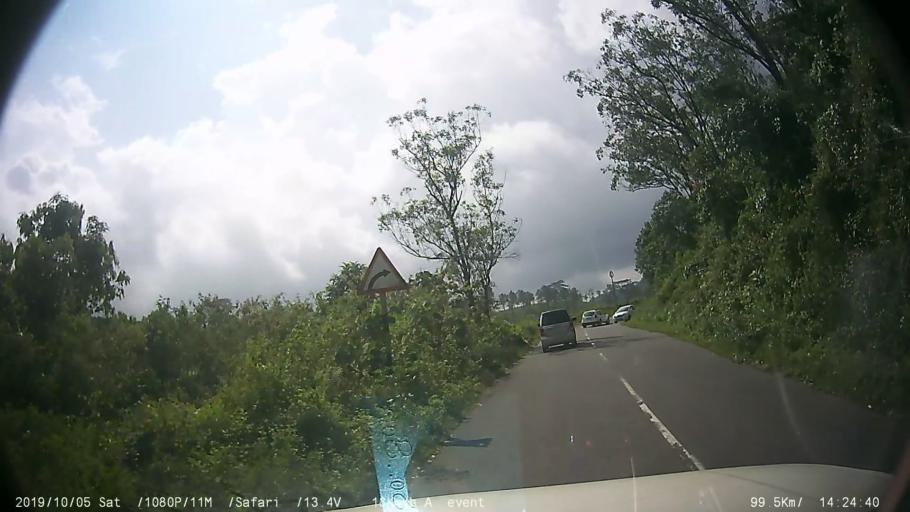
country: IN
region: Kerala
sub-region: Kottayam
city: Erattupetta
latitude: 9.5939
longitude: 76.9705
